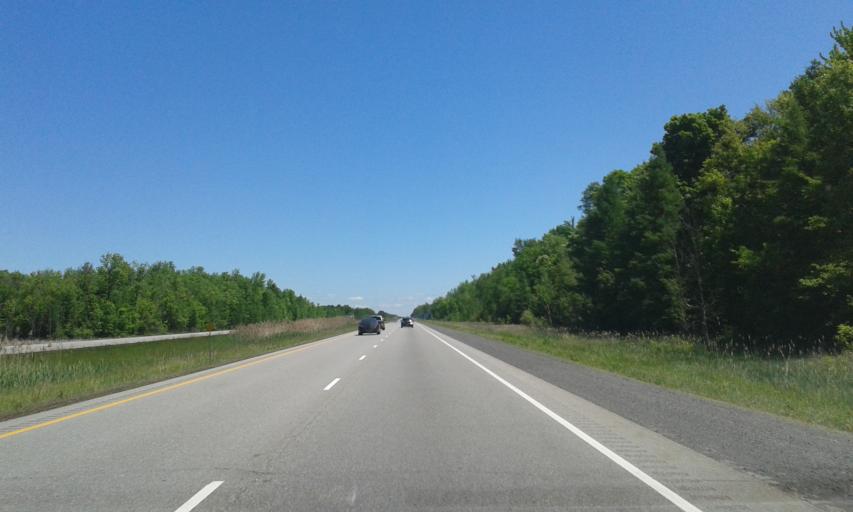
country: CA
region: Ontario
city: Prescott
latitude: 44.7910
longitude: -75.4364
